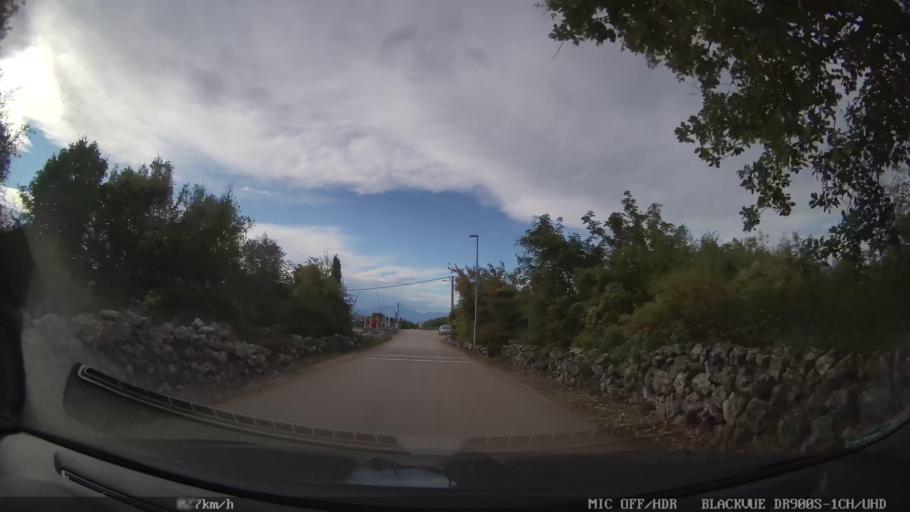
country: HR
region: Primorsko-Goranska
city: Njivice
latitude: 45.0808
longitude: 14.4457
